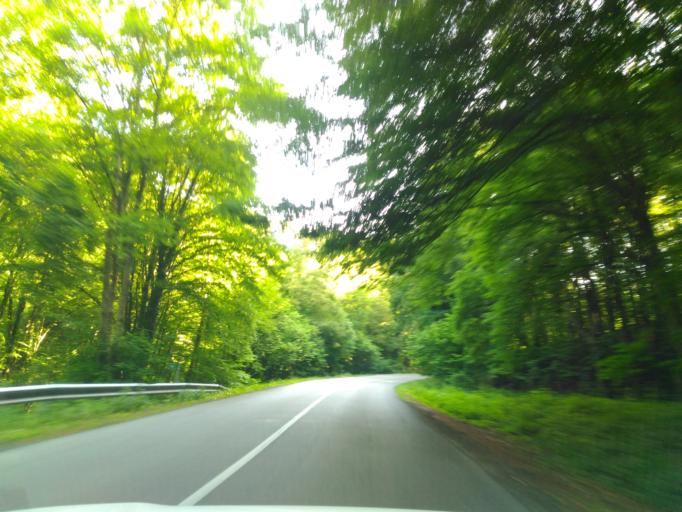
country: HU
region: Baranya
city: Komlo
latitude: 46.2090
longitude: 18.3000
